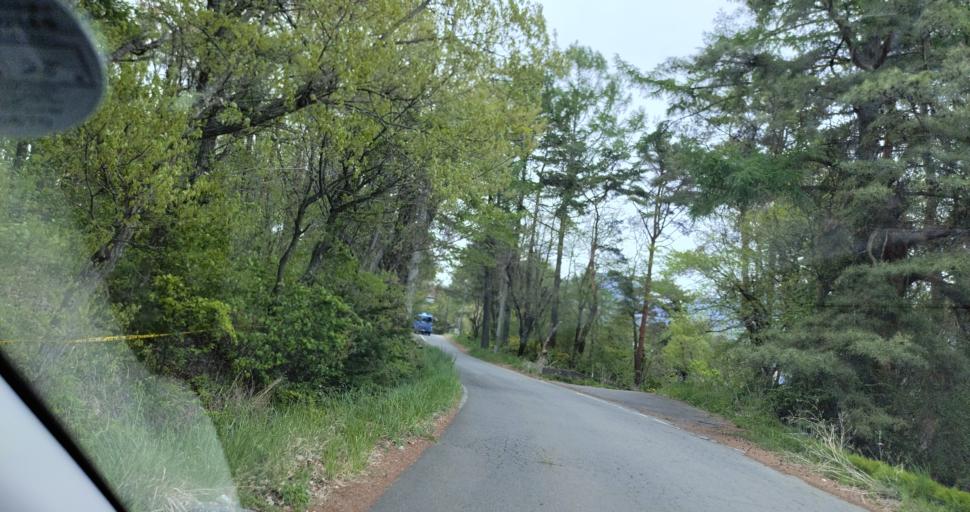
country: JP
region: Nagano
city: Komoro
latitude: 36.3397
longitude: 138.4681
